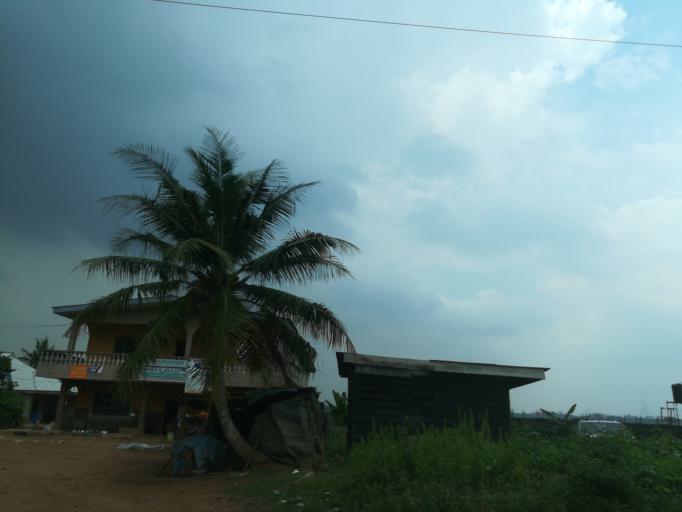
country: NG
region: Lagos
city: Ikorodu
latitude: 6.6029
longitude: 3.5872
